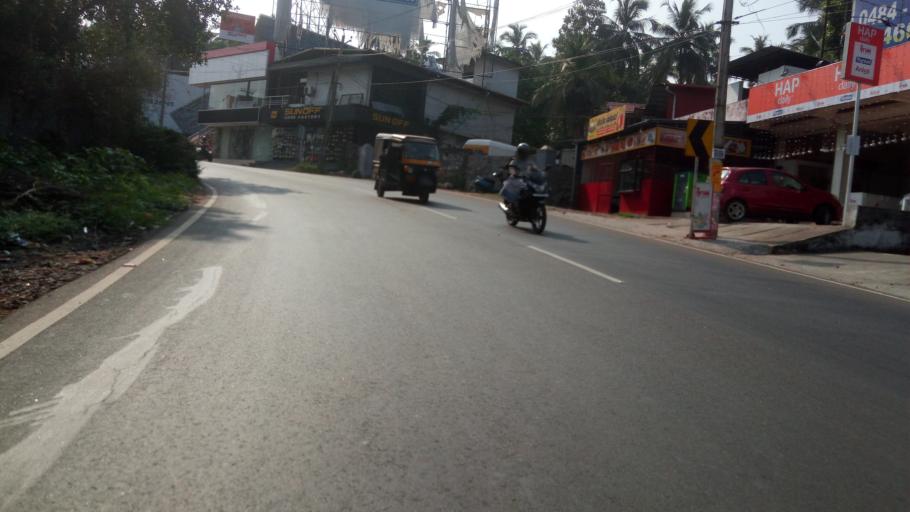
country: IN
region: Kerala
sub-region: Malappuram
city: Malappuram
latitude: 11.0037
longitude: 76.0099
